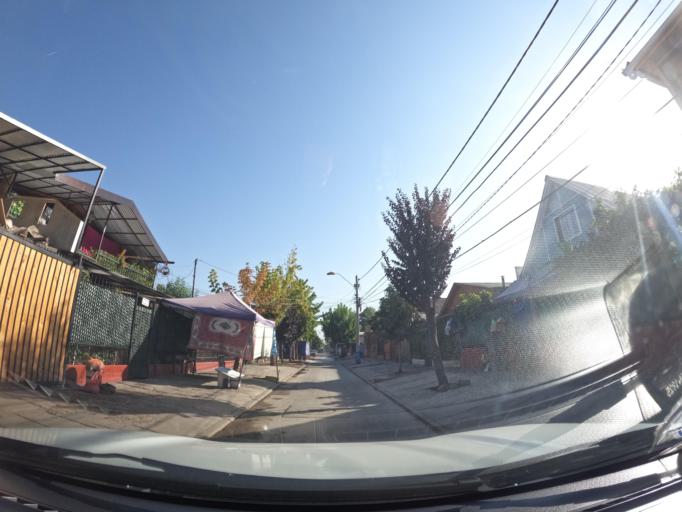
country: CL
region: Santiago Metropolitan
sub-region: Provincia de Santiago
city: Villa Presidente Frei, Nunoa, Santiago, Chile
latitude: -33.5103
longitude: -70.5661
